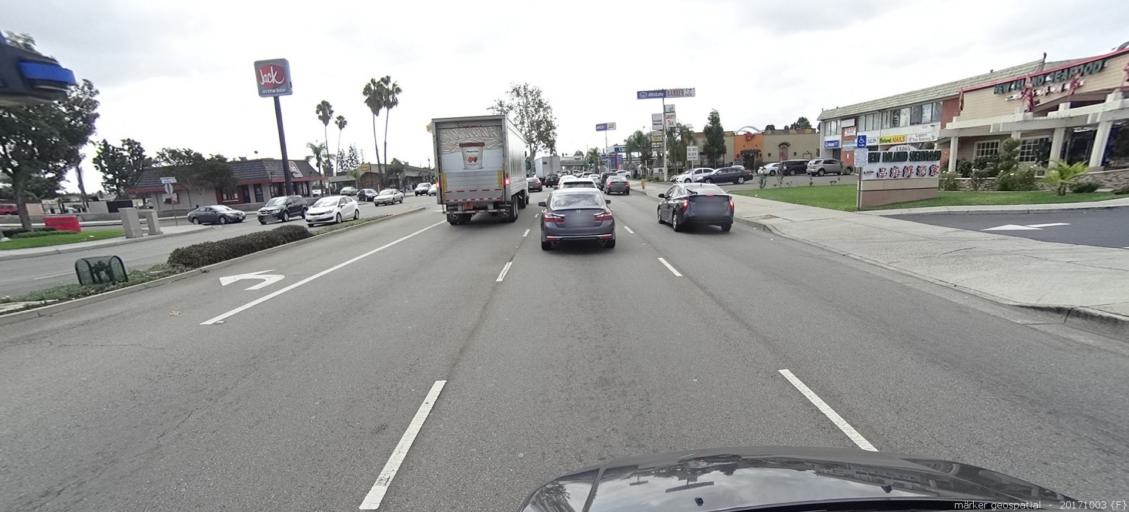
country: US
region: California
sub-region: Orange County
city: Garden Grove
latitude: 33.7708
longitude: -117.9205
